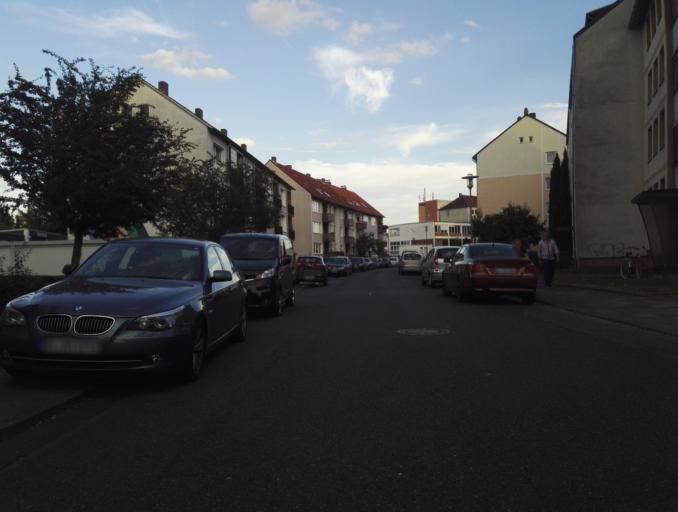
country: DE
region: Lower Saxony
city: Hildesheim
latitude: 52.1600
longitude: 9.9639
